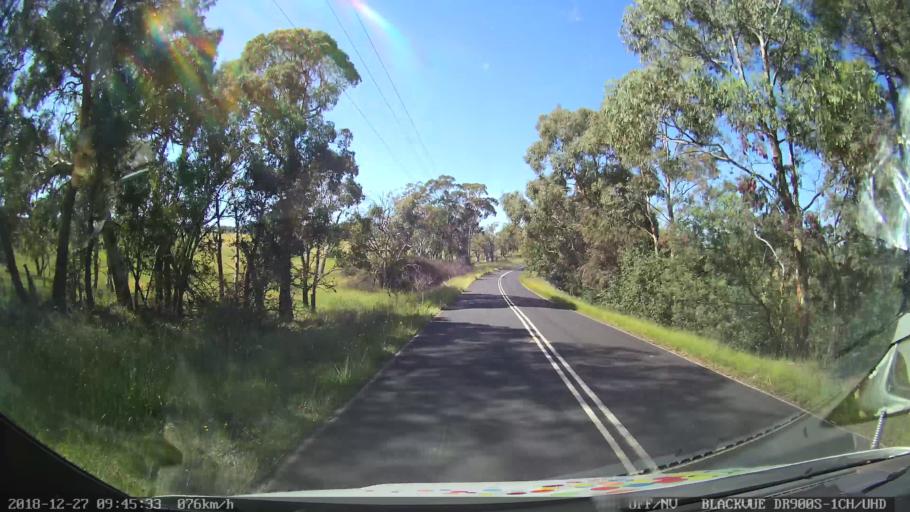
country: AU
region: New South Wales
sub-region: Lithgow
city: Portland
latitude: -33.3258
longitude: 149.9844
